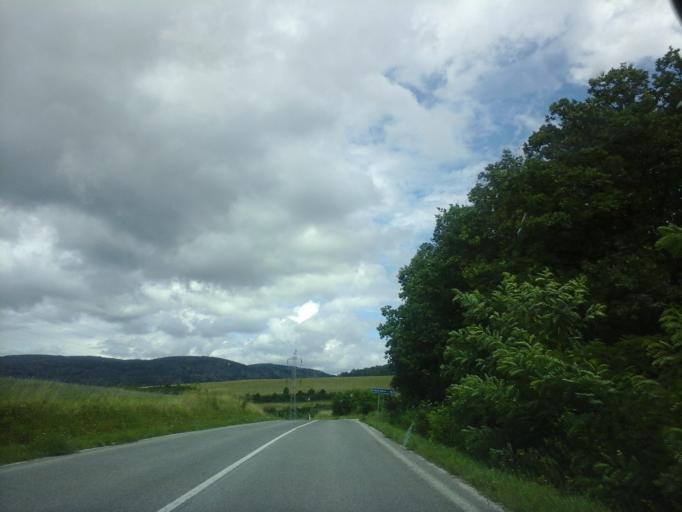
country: SK
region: Kosicky
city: Roznava
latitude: 48.5332
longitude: 20.4111
